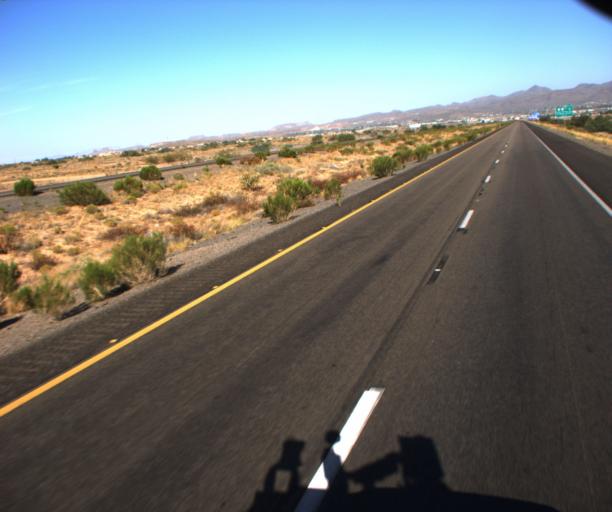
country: US
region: Arizona
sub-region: Mohave County
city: New Kingman-Butler
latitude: 35.2125
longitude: -113.9746
